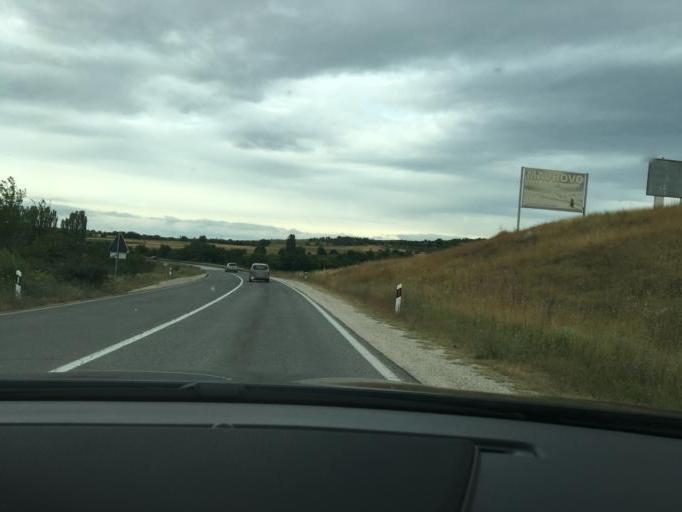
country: MK
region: Staro Nagoricane
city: Staro Nagorichane
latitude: 42.1712
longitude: 21.8052
